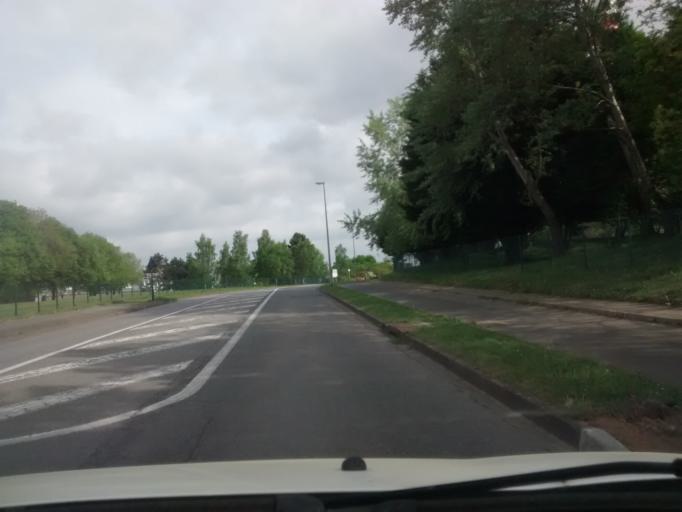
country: FR
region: Brittany
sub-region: Departement d'Ille-et-Vilaine
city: Cesson-Sevigne
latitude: 48.1229
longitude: -1.6285
